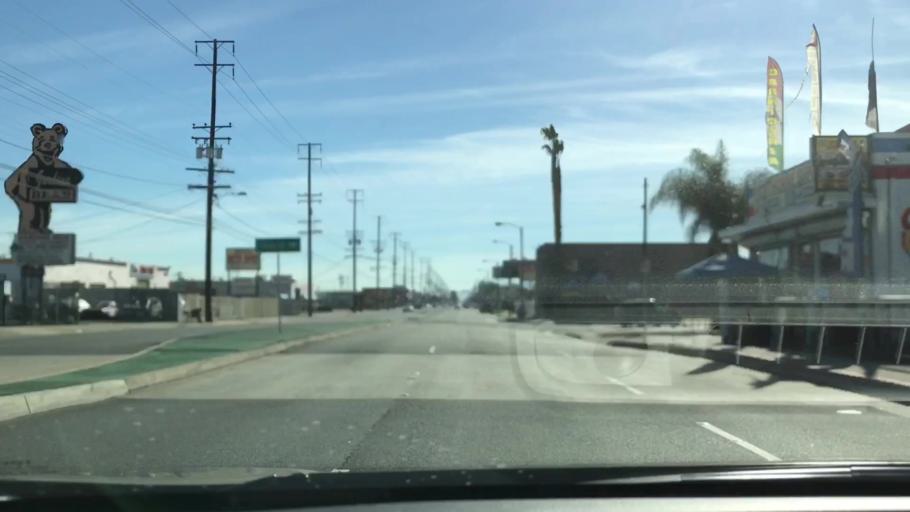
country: US
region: California
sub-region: Los Angeles County
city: Alondra Park
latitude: 33.9129
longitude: -118.3266
